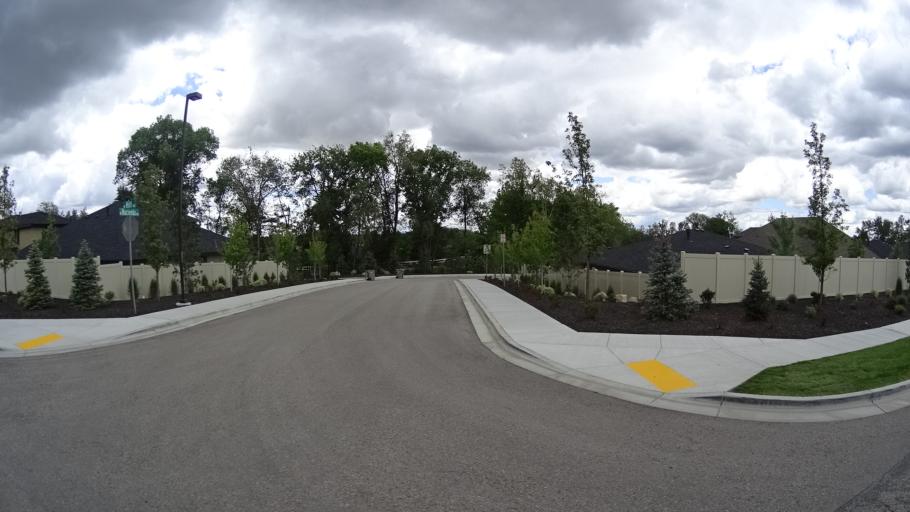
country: US
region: Idaho
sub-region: Ada County
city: Garden City
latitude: 43.6767
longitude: -116.2649
